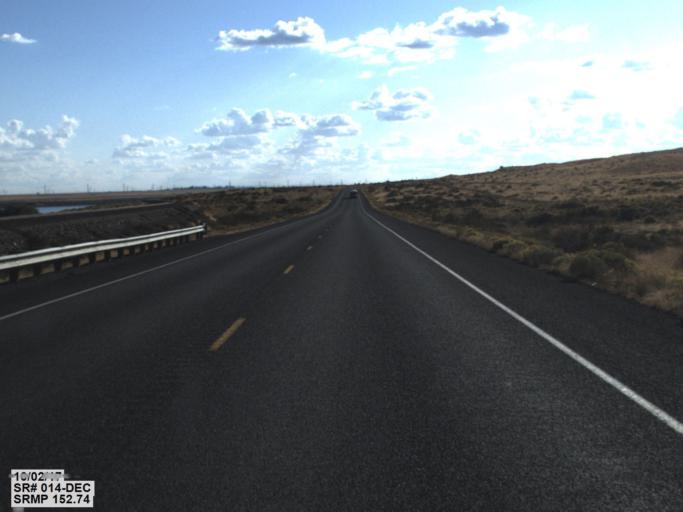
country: US
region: Oregon
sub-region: Morrow County
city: Boardman
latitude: 45.8535
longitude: -119.8631
